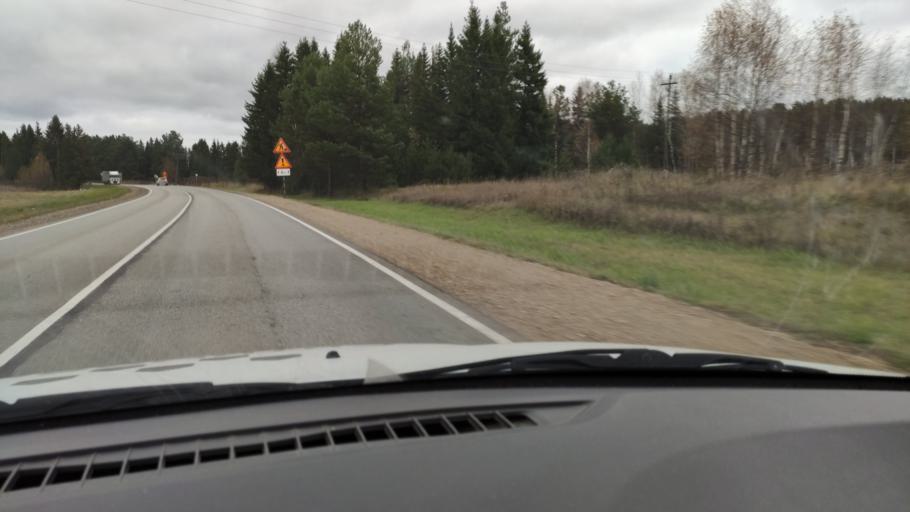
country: RU
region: Kirov
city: Slobodskoy
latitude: 58.7797
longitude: 50.4419
